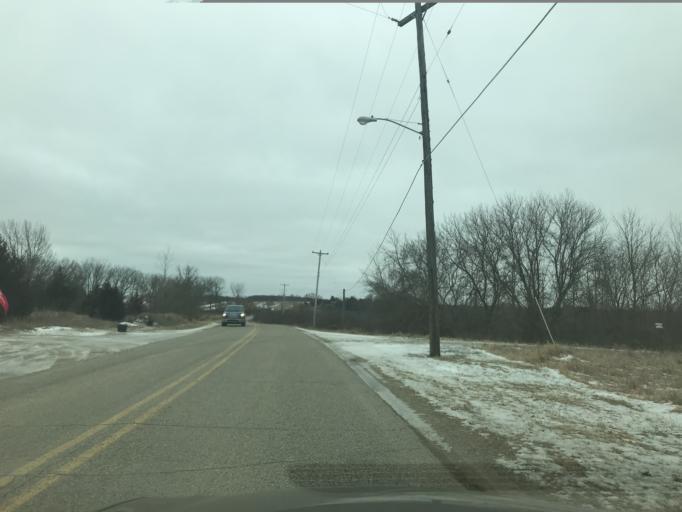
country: US
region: Michigan
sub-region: Jackson County
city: Brooklyn
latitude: 42.0640
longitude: -84.3259
